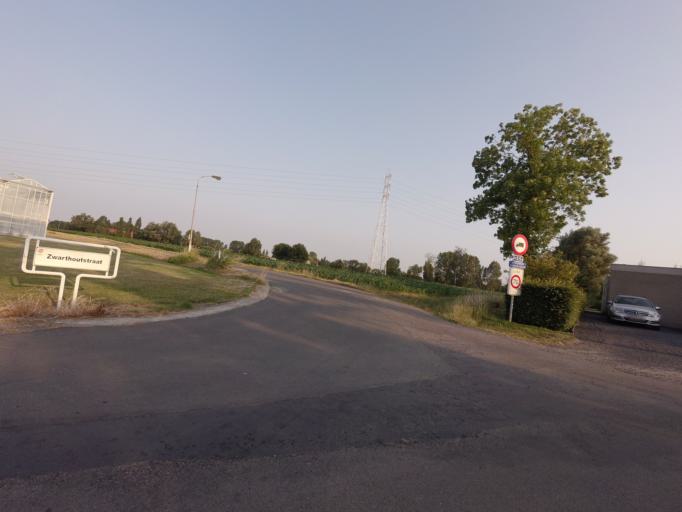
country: BE
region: Flanders
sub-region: Provincie Antwerpen
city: Lint
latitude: 51.1062
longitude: 4.4742
